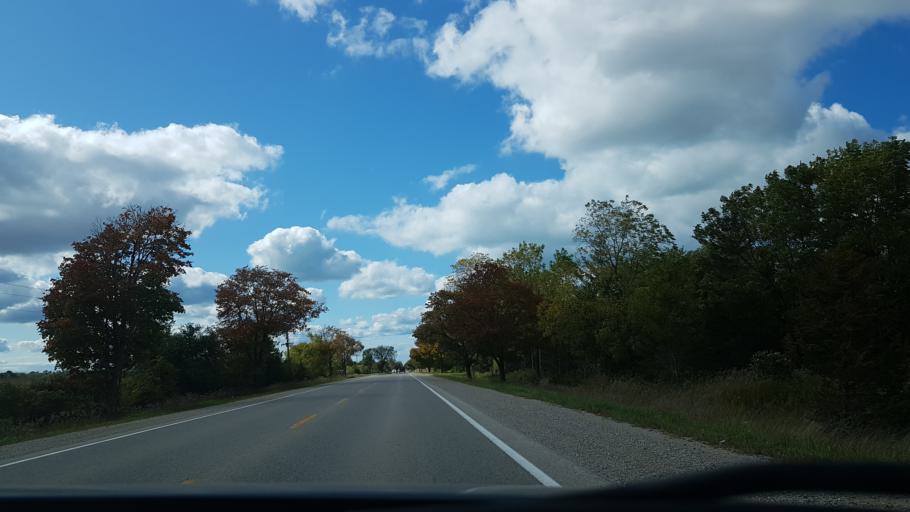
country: CA
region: Ontario
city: Bluewater
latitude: 43.3415
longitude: -81.6793
